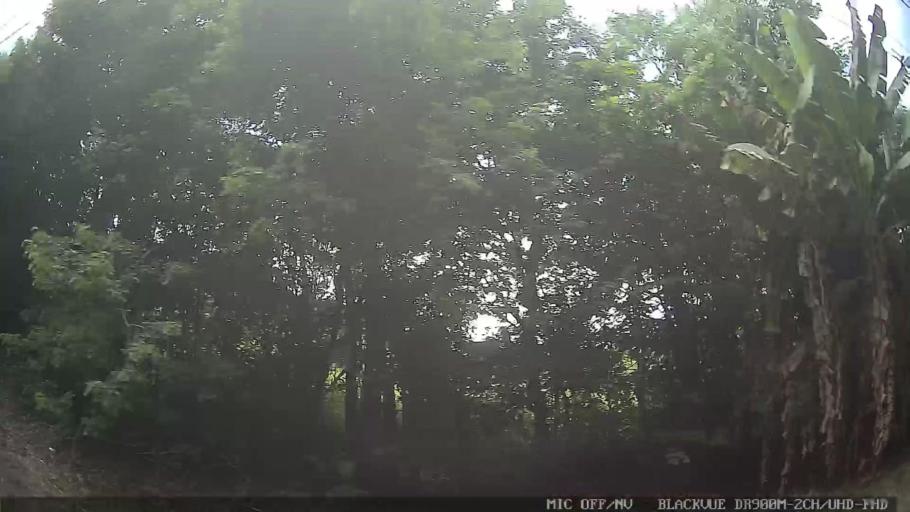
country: BR
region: Sao Paulo
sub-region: Santa Isabel
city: Santa Isabel
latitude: -23.3999
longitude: -46.1968
